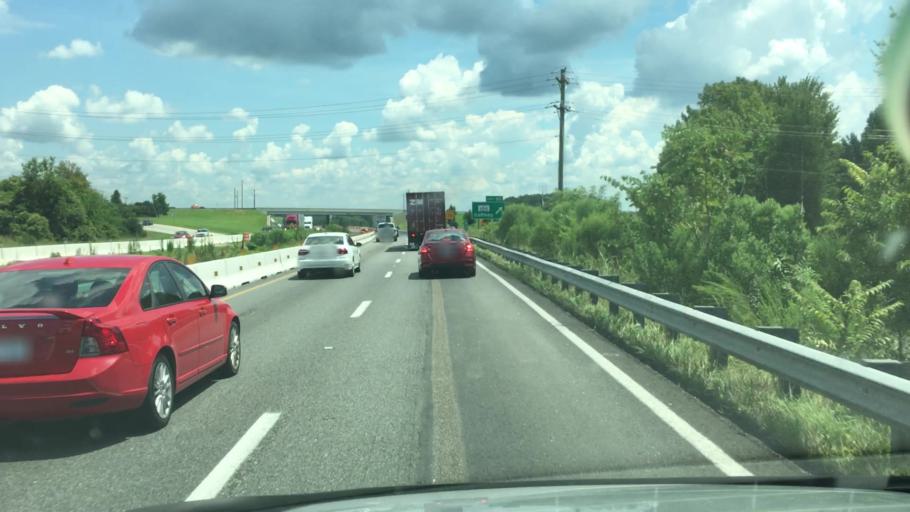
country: US
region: South Carolina
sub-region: Cherokee County
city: Gaffney
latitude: 35.0812
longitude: -81.7117
